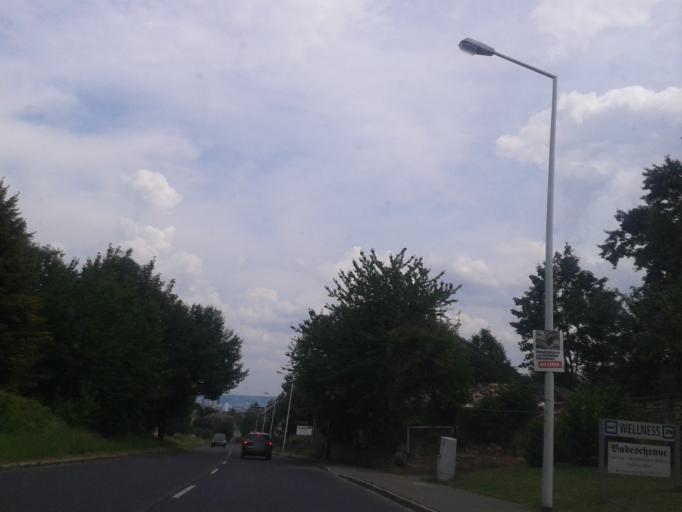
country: DE
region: Saxony
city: Freital
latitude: 51.0400
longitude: 13.6695
